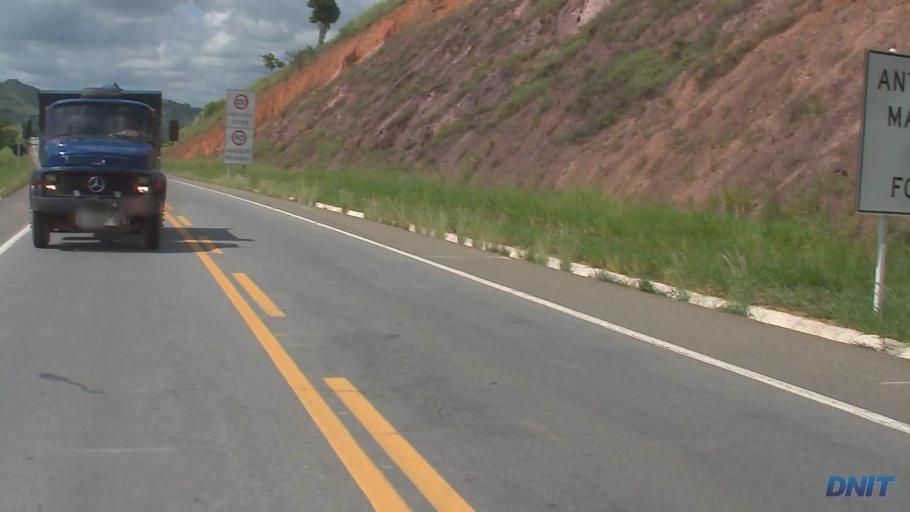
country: BR
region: Minas Gerais
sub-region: Belo Oriente
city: Belo Oriente
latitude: -19.1286
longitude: -42.2135
